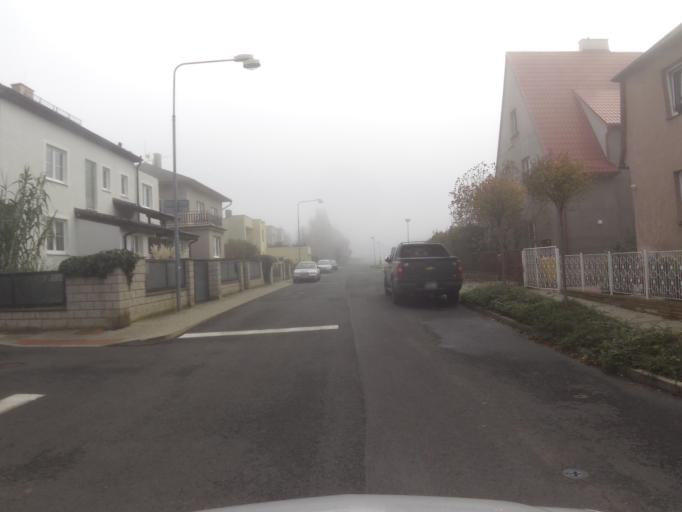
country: CZ
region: Ustecky
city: Zatec
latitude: 50.3195
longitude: 13.5526
